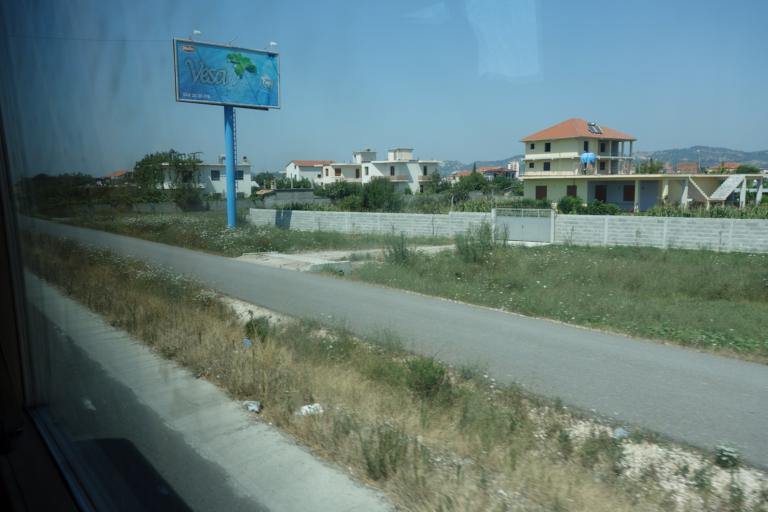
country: AL
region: Tirane
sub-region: Rrethi i Kavajes
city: Synej
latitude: 41.1863
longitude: 19.5426
